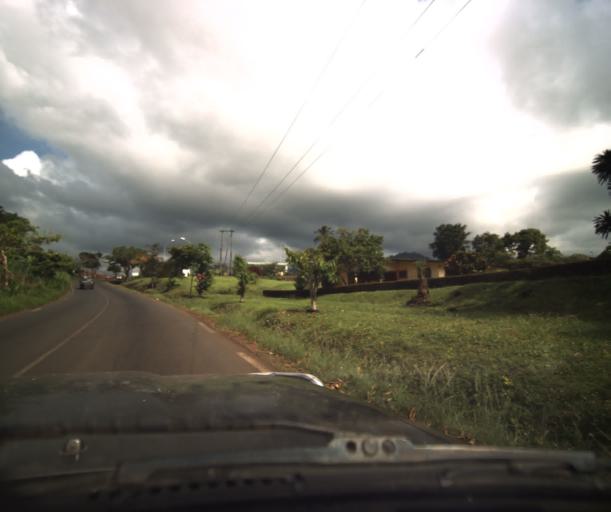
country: CM
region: South-West Province
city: Limbe
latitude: 4.0193
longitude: 9.1828
